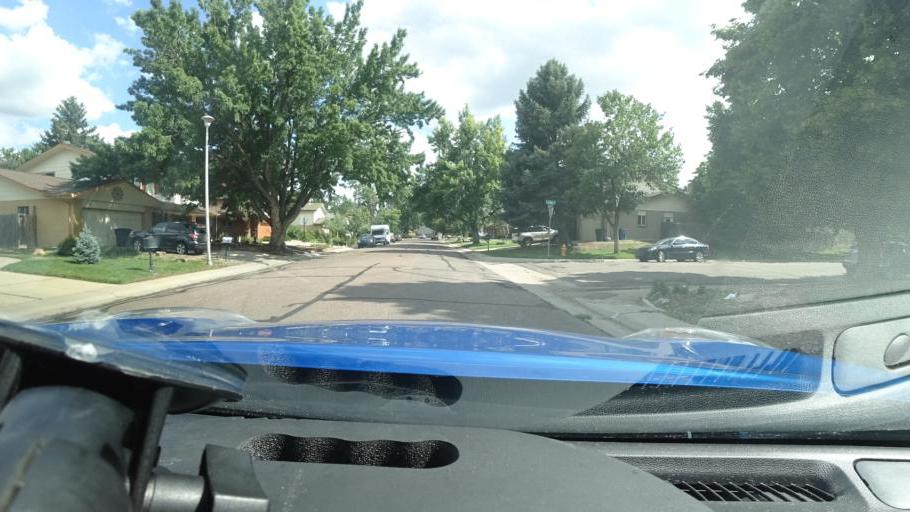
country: US
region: Colorado
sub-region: Adams County
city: Aurora
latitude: 39.6911
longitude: -104.8575
